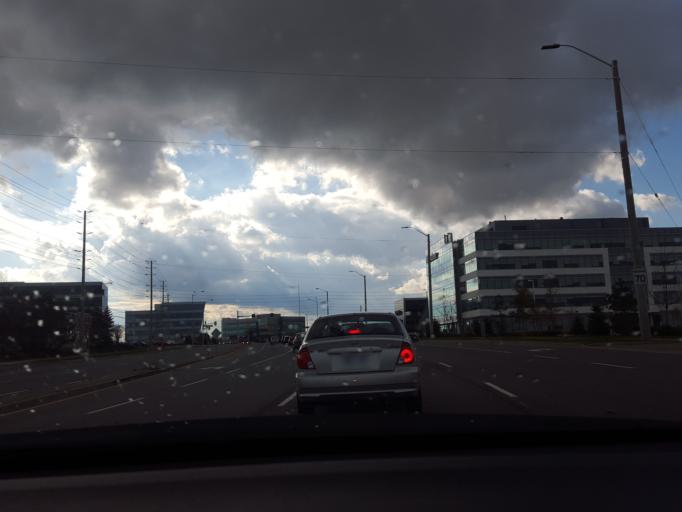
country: CA
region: Ontario
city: Brampton
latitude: 43.6113
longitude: -79.7504
